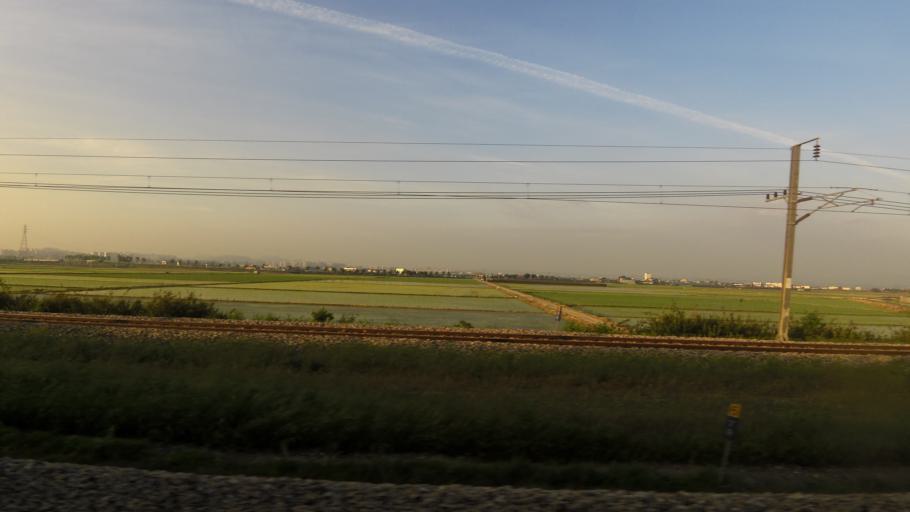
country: KR
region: Chungcheongnam-do
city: Seonghwan
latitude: 36.9604
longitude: 127.1143
